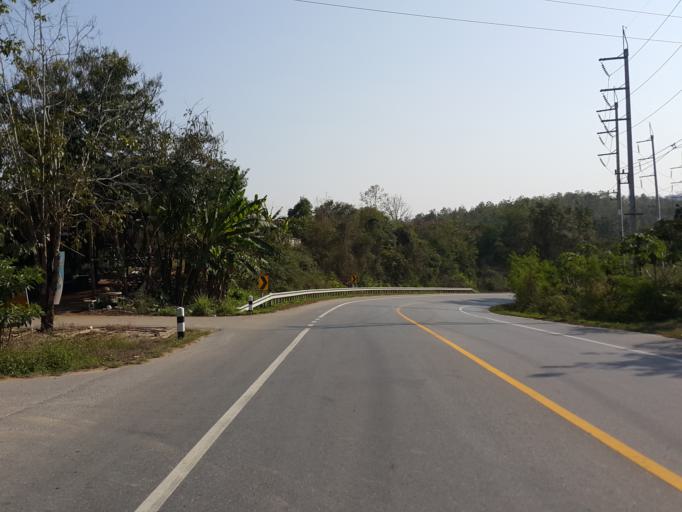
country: TH
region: Lampang
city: Chae Hom
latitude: 18.6226
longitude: 99.5445
